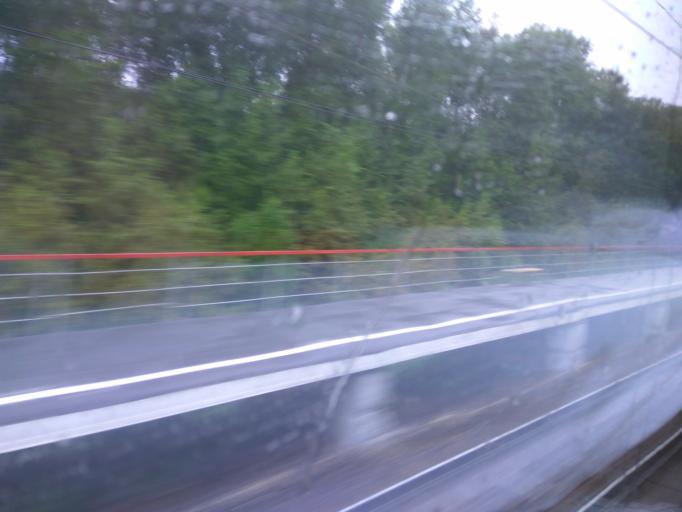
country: RU
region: Moskovskaya
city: Zhilevo
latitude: 55.0260
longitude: 38.0103
